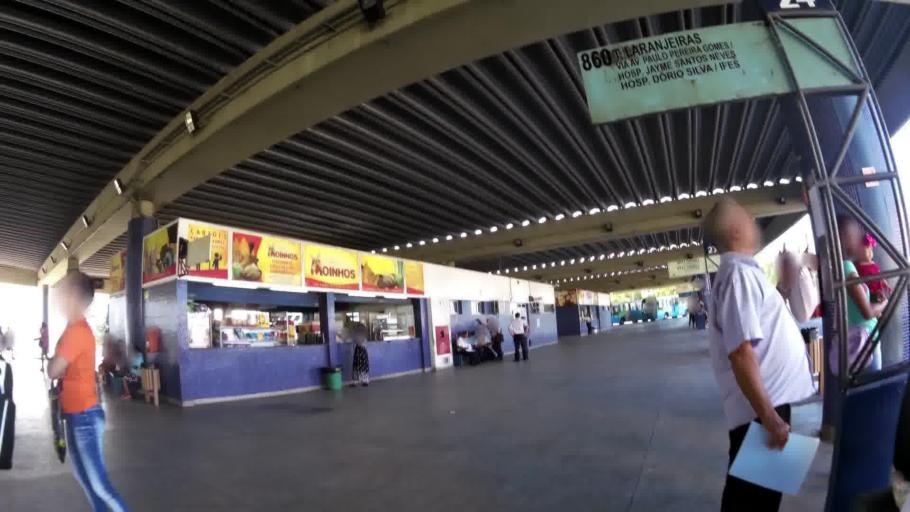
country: BR
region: Espirito Santo
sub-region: Serra
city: Serra
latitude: -20.1591
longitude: -40.1956
